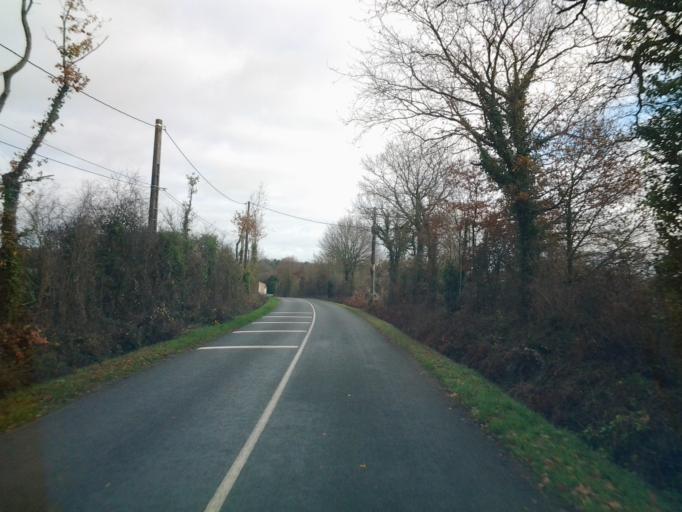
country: FR
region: Pays de la Loire
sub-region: Departement de la Vendee
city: Saint-Florent-des-Bois
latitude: 46.6342
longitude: -1.3510
